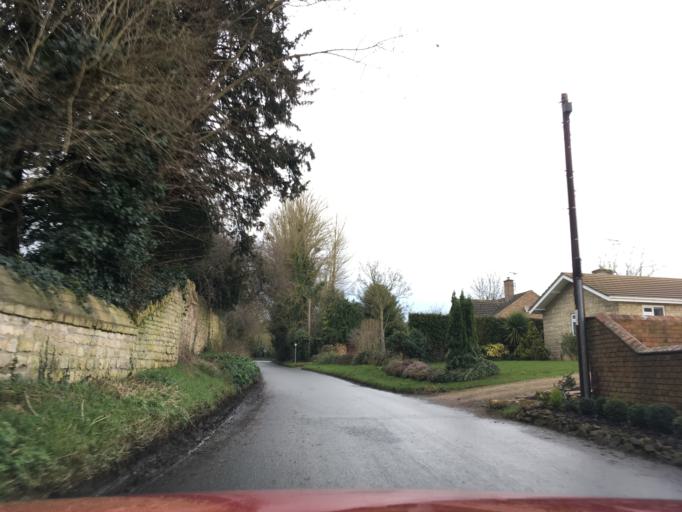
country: GB
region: England
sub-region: Gloucestershire
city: Gotherington
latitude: 52.0212
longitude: -2.0336
